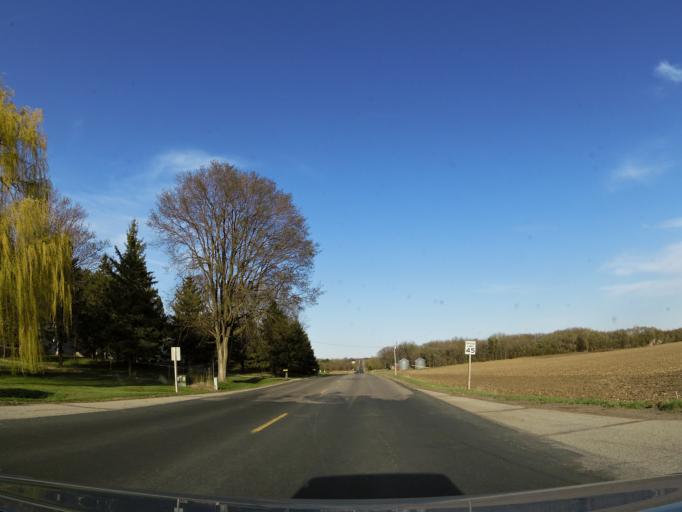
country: US
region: Wisconsin
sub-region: Pierce County
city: River Falls
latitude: 44.8626
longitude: -92.6649
